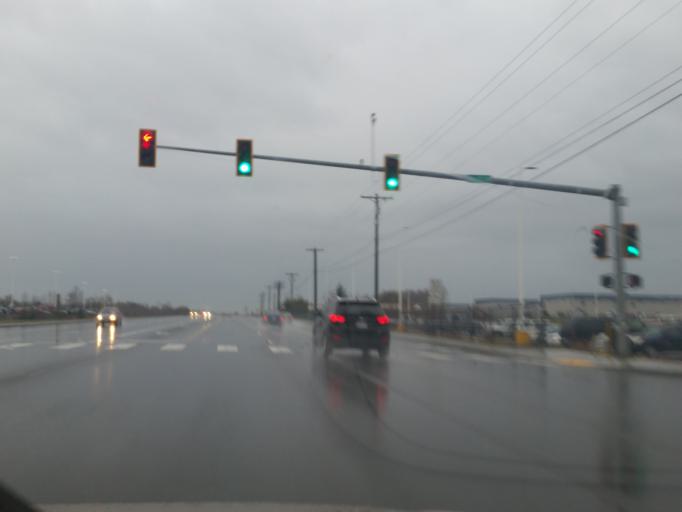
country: US
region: Washington
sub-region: Snohomish County
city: Mukilteo
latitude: 47.9134
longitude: -122.2718
